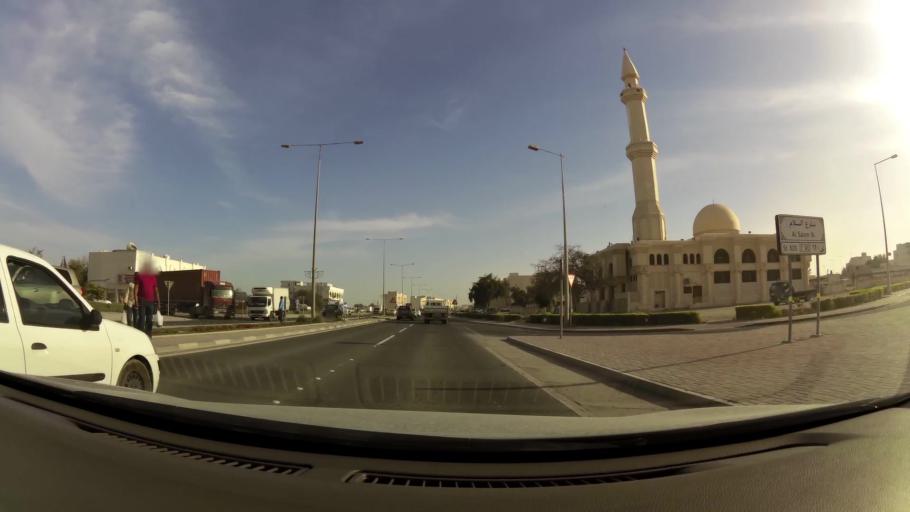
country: QA
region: Al Wakrah
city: Al Wakrah
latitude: 25.1679
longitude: 51.6076
